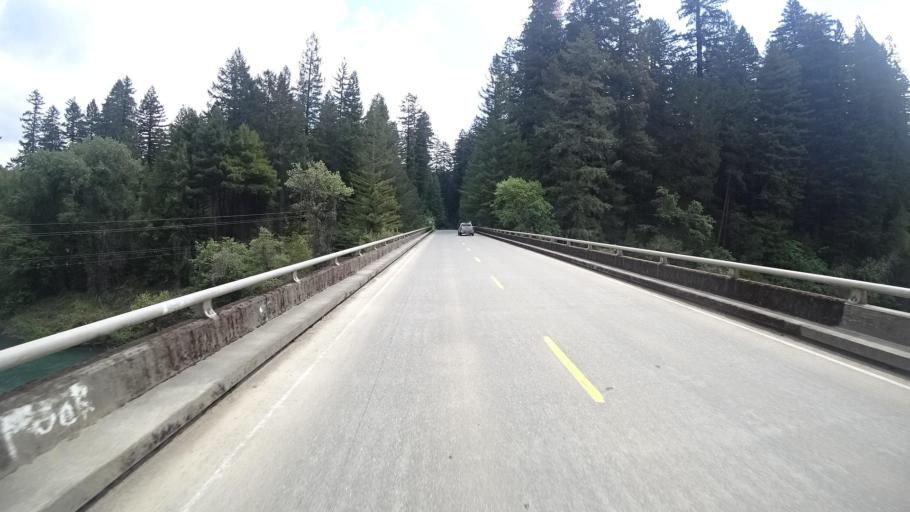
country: US
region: California
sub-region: Humboldt County
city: Redway
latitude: 40.1221
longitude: -123.8366
